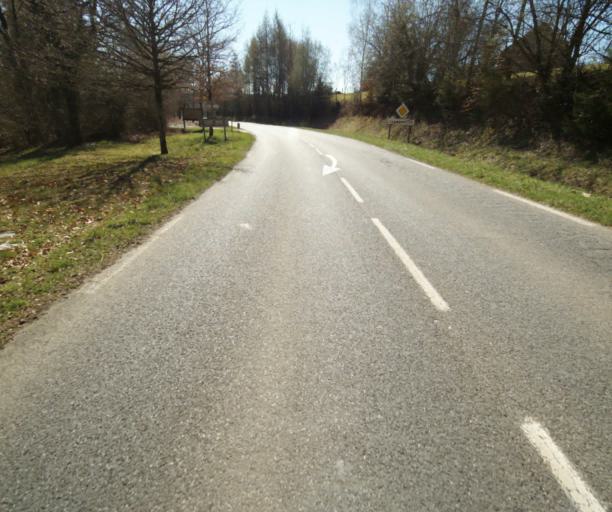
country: FR
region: Limousin
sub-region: Departement de la Correze
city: Chamboulive
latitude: 45.4240
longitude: 1.7109
